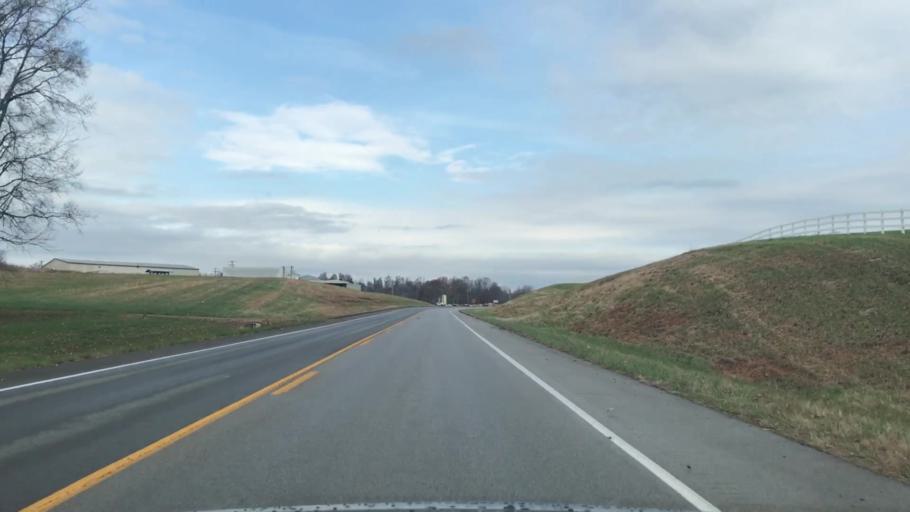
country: US
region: Kentucky
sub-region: Monroe County
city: Tompkinsville
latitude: 36.7493
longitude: -85.6910
